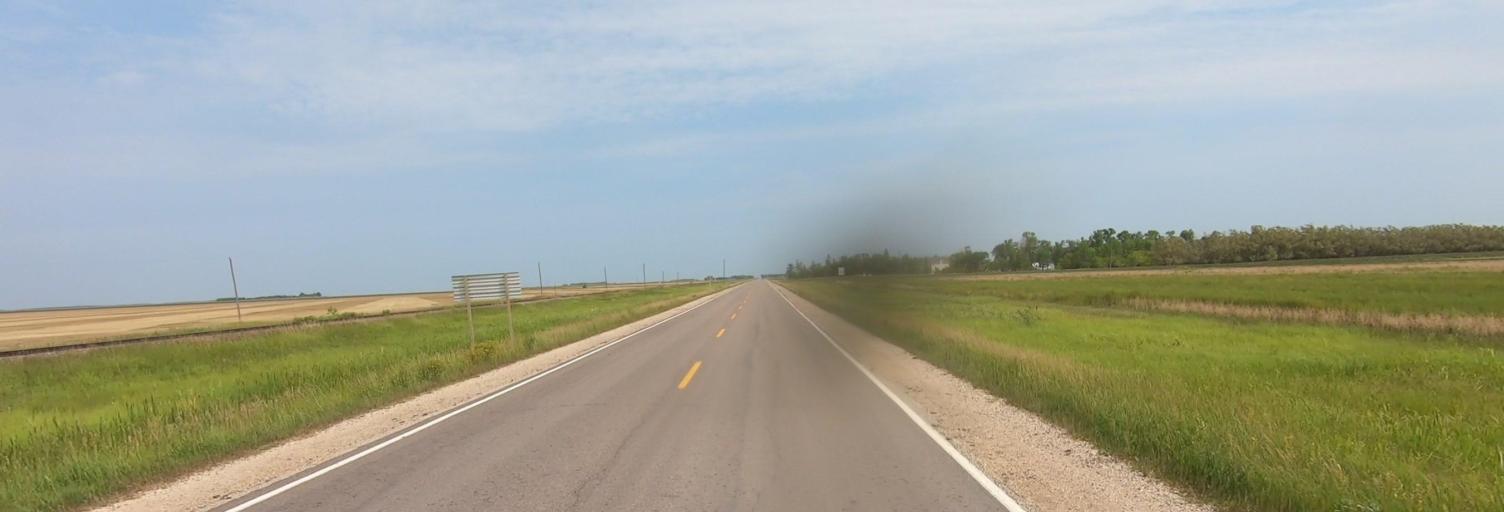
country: CA
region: Manitoba
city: Morris
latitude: 49.5777
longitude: -97.3474
